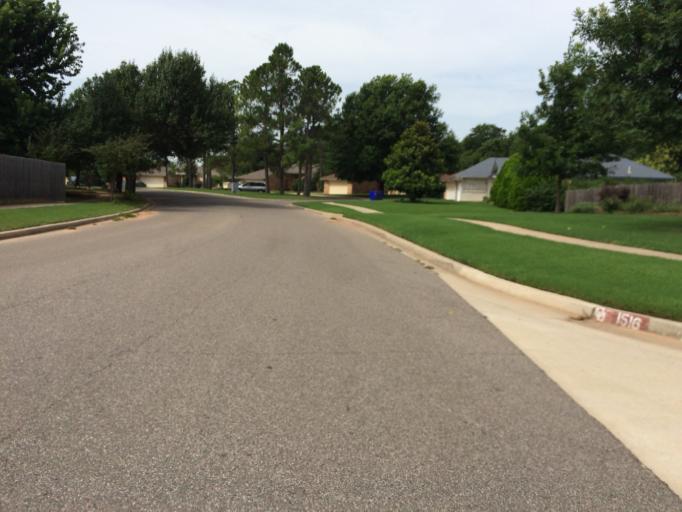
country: US
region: Oklahoma
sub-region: Cleveland County
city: Norman
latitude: 35.2002
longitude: -97.4167
